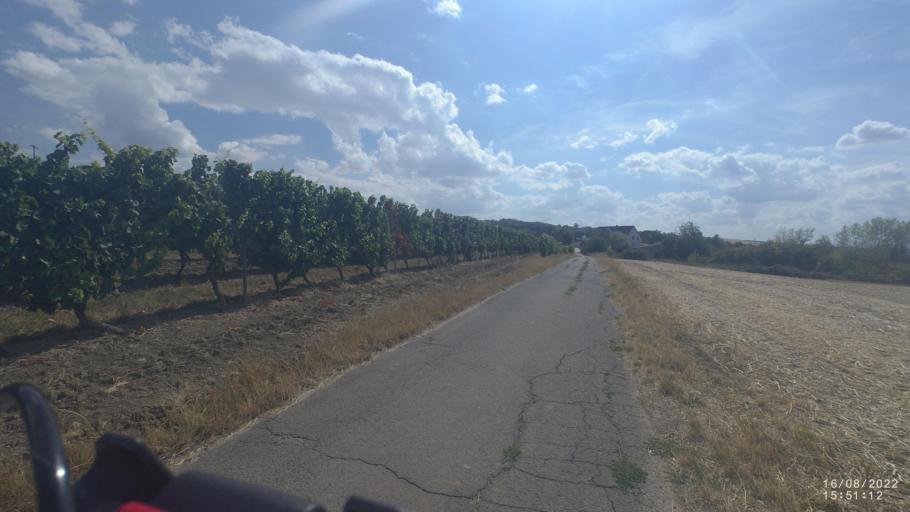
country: DE
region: Rheinland-Pfalz
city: Sulzheim
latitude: 49.8264
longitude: 8.0944
